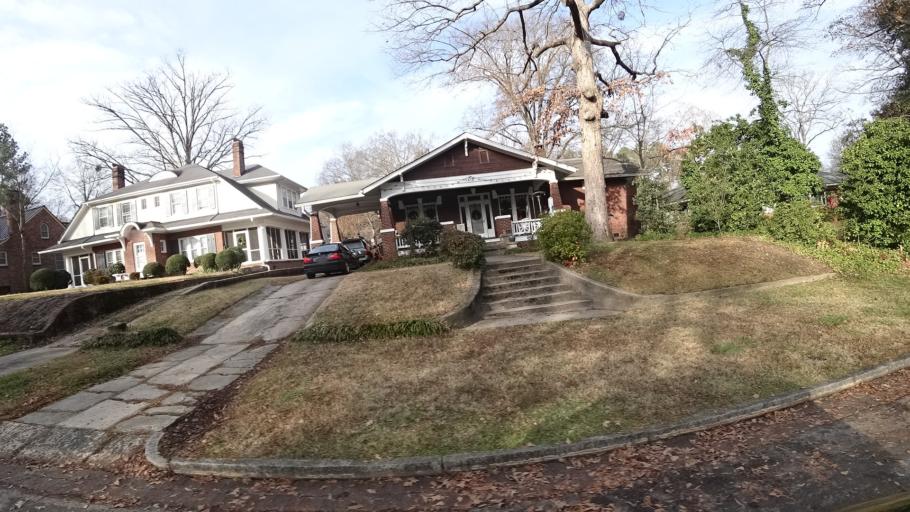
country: US
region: North Carolina
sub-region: Durham County
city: Durham
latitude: 36.0109
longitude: -78.8928
